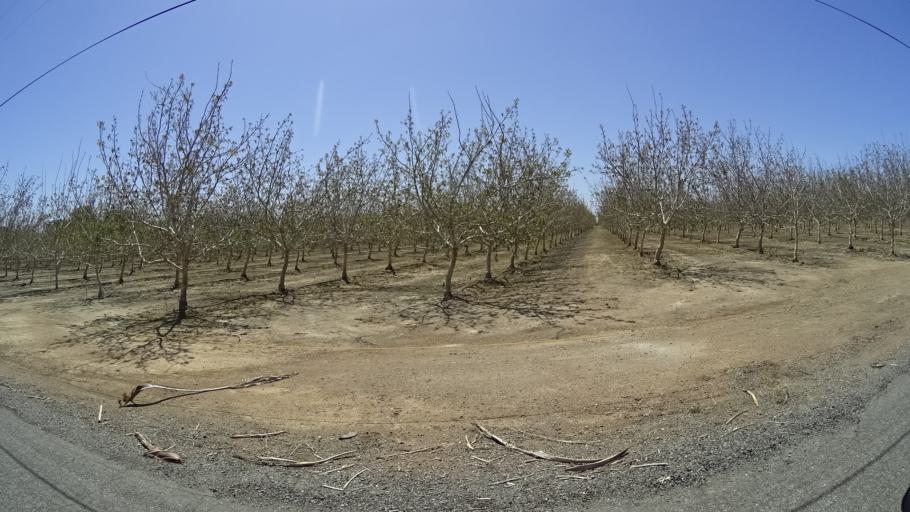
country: US
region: California
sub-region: Glenn County
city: Orland
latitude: 39.7962
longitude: -122.1810
